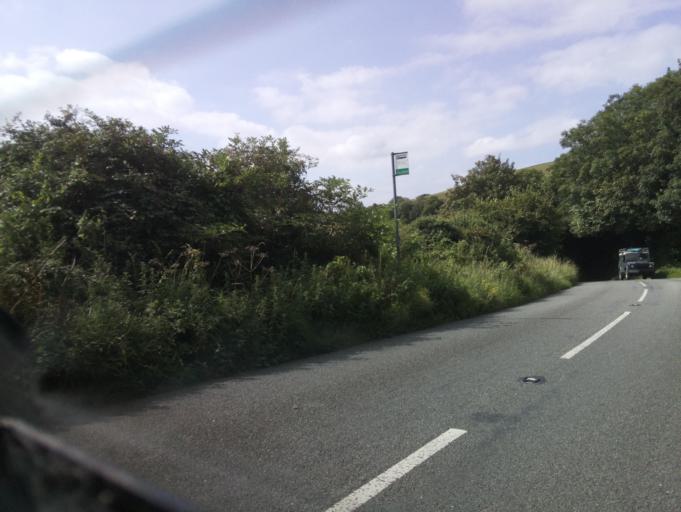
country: GB
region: England
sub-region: Devon
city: Dartmouth
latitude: 50.3635
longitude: -3.5596
